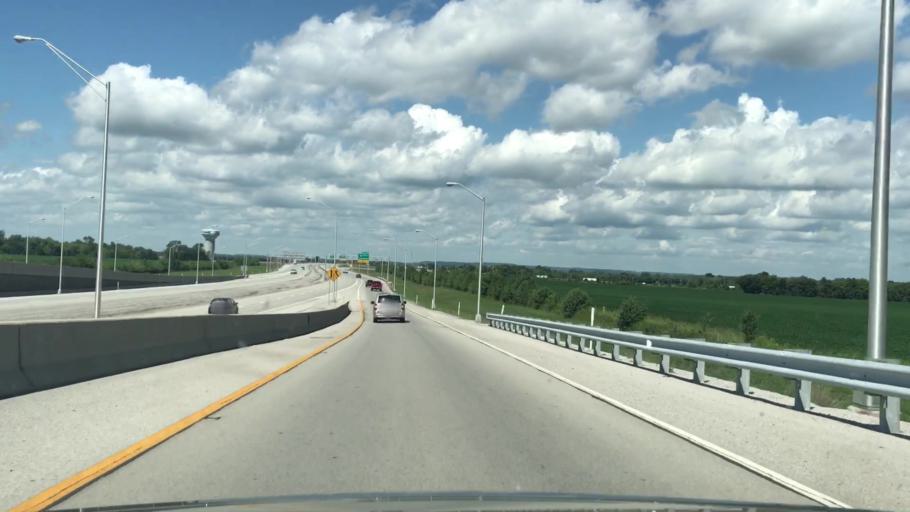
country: US
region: Kentucky
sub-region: Warren County
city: Plano
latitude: 36.9079
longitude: -86.4197
